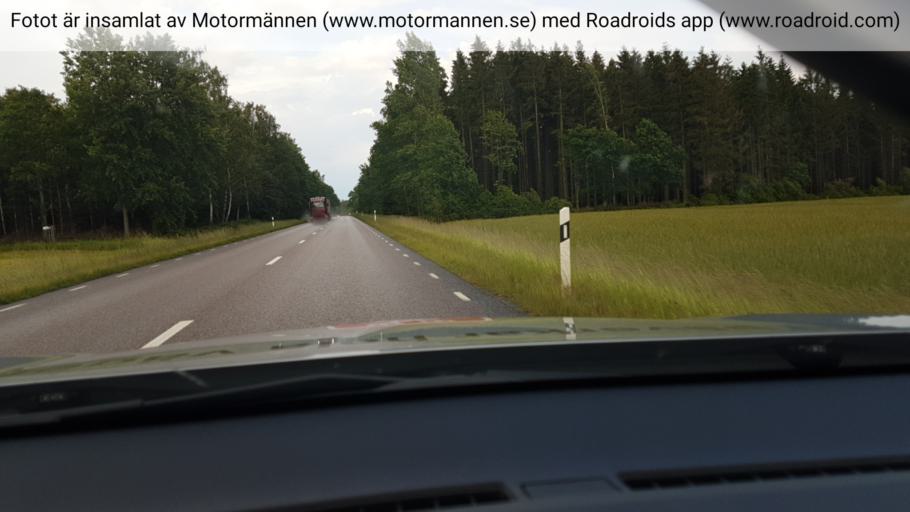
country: SE
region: Vaestra Goetaland
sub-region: Hjo Kommun
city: Hjo
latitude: 58.2582
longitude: 14.2445
